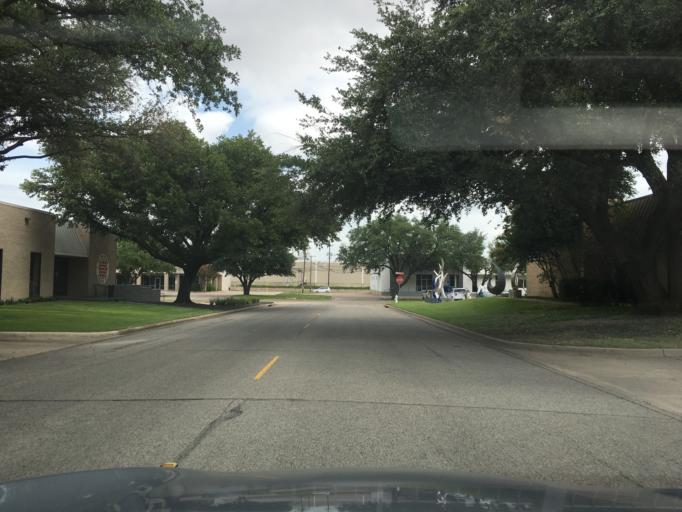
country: US
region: Texas
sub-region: Dallas County
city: Addison
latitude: 32.9359
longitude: -96.8320
